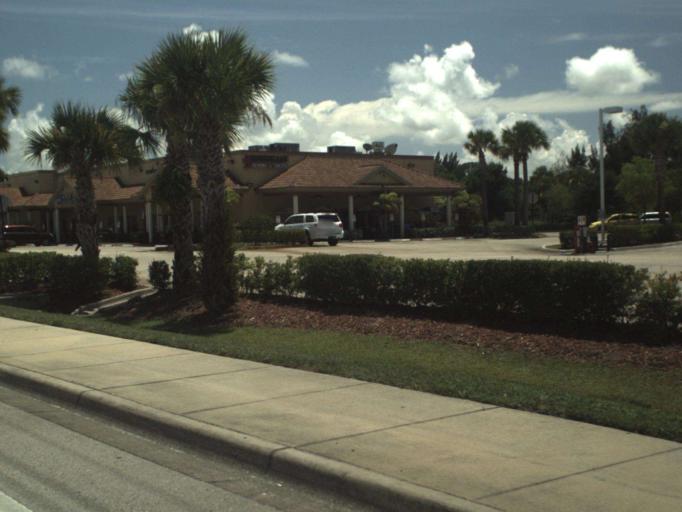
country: US
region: Florida
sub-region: Saint Lucie County
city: Indian River Estates
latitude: 27.3445
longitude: -80.3260
